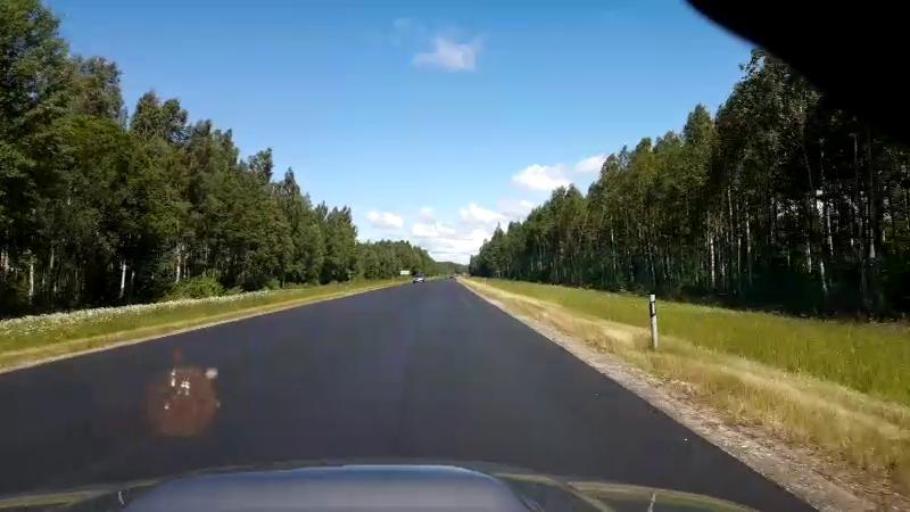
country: LV
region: Salacgrivas
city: Ainazi
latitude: 57.9731
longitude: 24.4528
